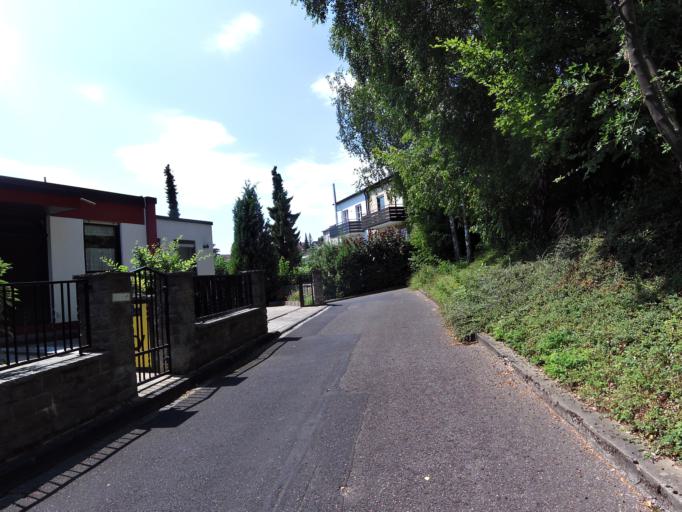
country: DE
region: Bavaria
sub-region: Regierungsbezirk Unterfranken
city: Wuerzburg
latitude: 49.8054
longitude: 9.9762
